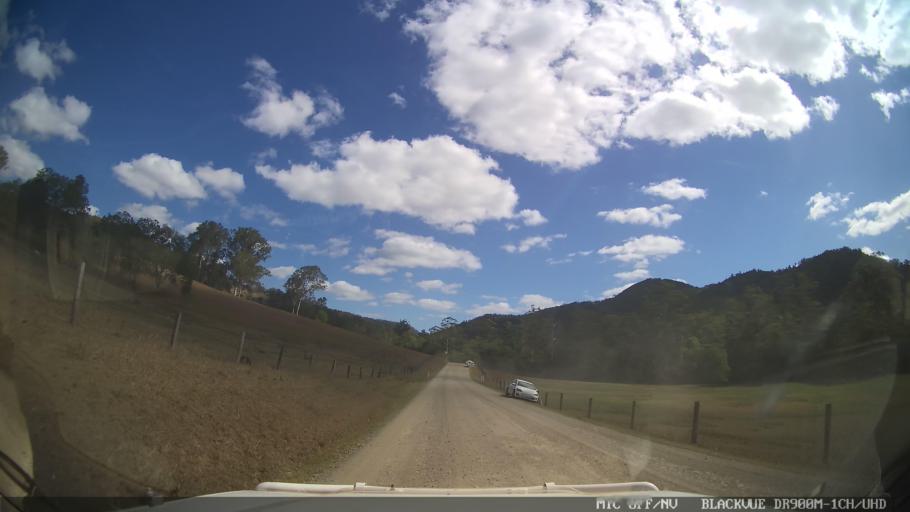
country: AU
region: Queensland
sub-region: Sunshine Coast
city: Nambour
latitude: -26.6302
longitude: 152.6540
